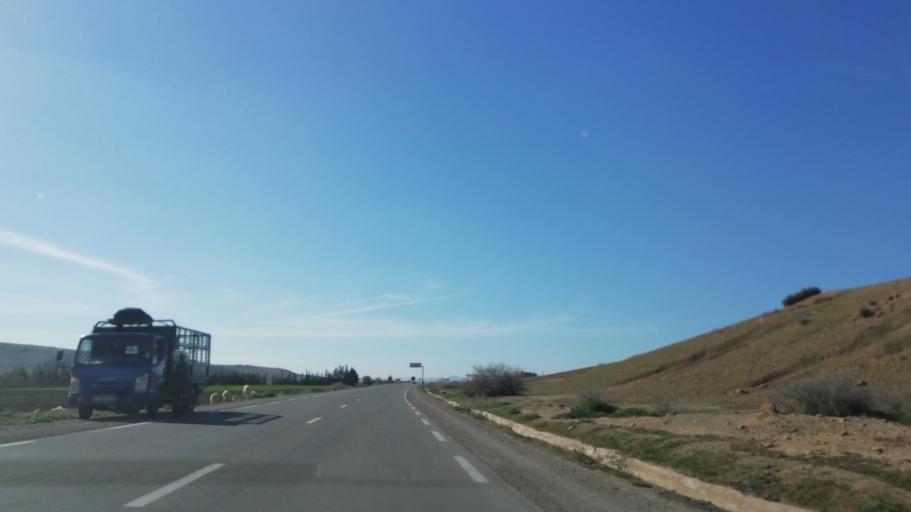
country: DZ
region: Mascara
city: Oued el Abtal
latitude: 35.4501
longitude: 0.7866
